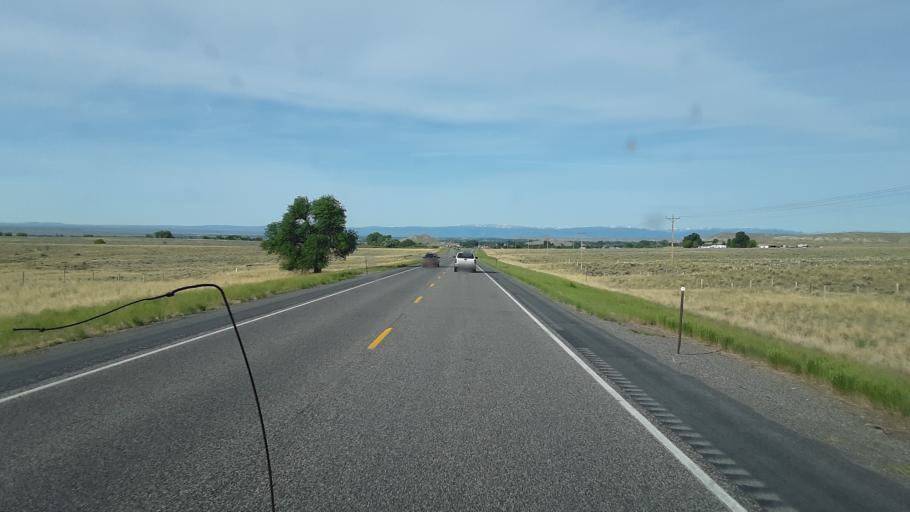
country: US
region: Wyoming
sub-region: Fremont County
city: Riverton
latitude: 43.1455
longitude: -108.2856
